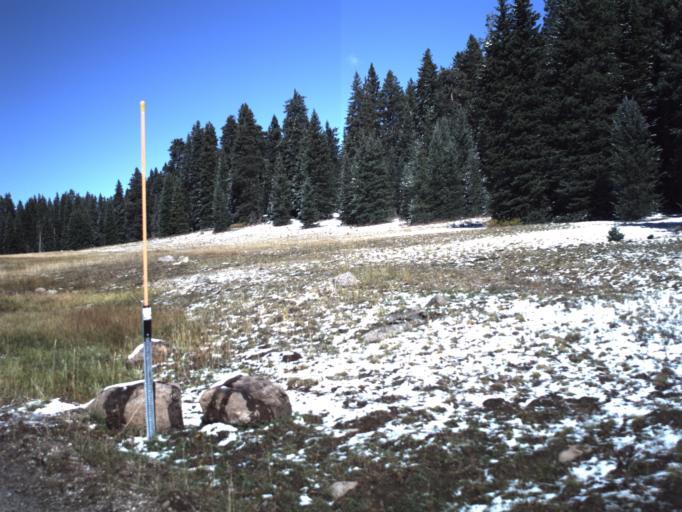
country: US
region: Utah
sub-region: Piute County
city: Junction
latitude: 38.2981
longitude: -112.3598
